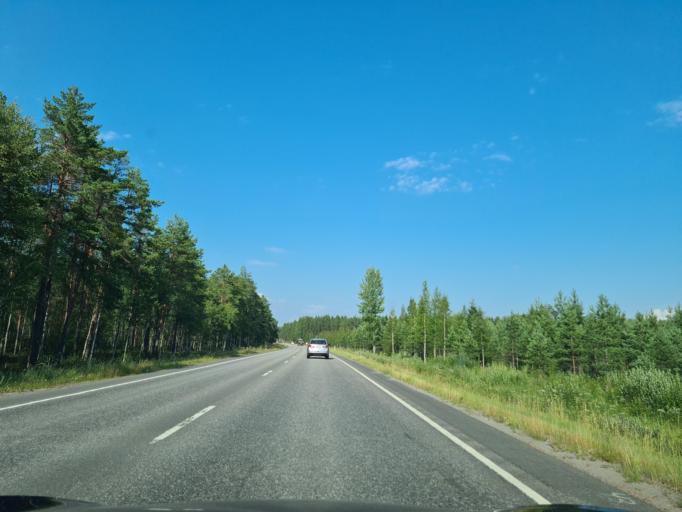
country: FI
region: Satakunta
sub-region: Pohjois-Satakunta
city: Kankaanpaeae
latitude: 61.8413
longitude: 22.4486
